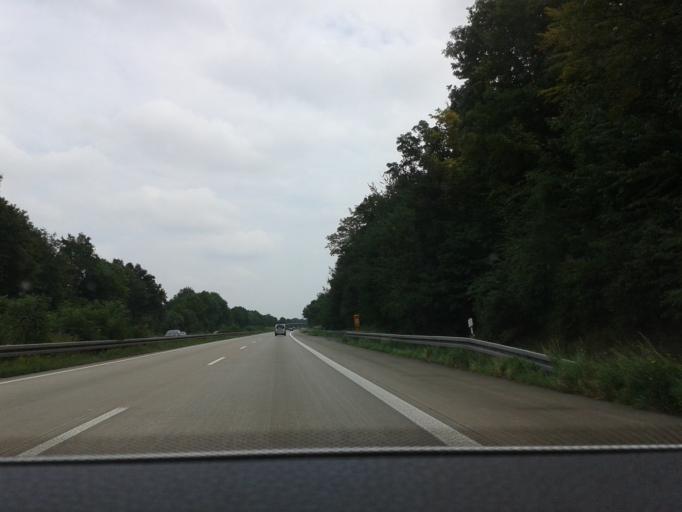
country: DE
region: North Rhine-Westphalia
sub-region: Regierungsbezirk Arnsberg
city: Soest
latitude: 51.5465
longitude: 8.0694
